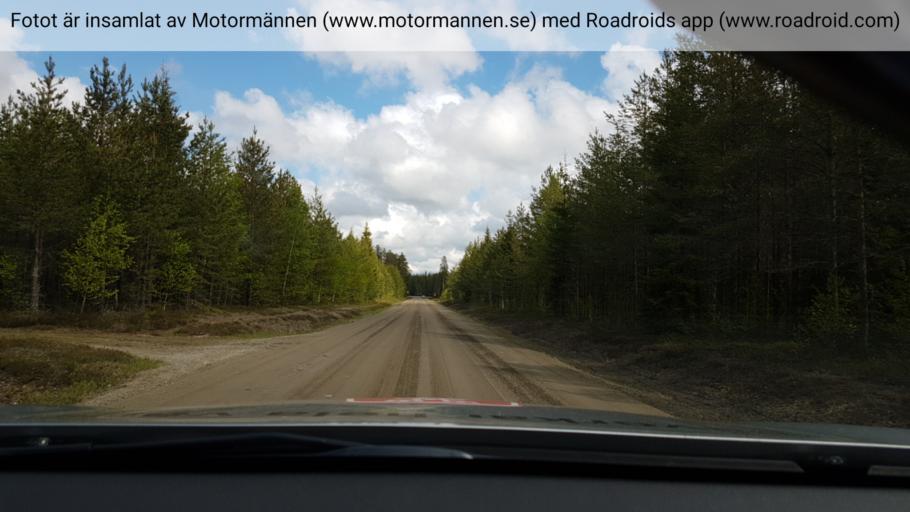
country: SE
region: Vaesterbotten
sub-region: Vindelns Kommun
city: Vindeln
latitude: 64.0815
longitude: 19.6188
